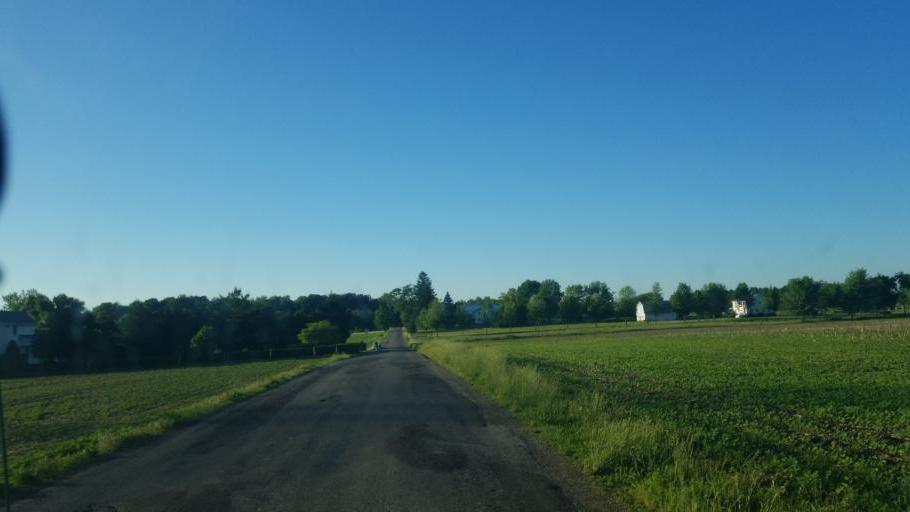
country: US
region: Indiana
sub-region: Elkhart County
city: Nappanee
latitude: 41.4285
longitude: -86.0493
